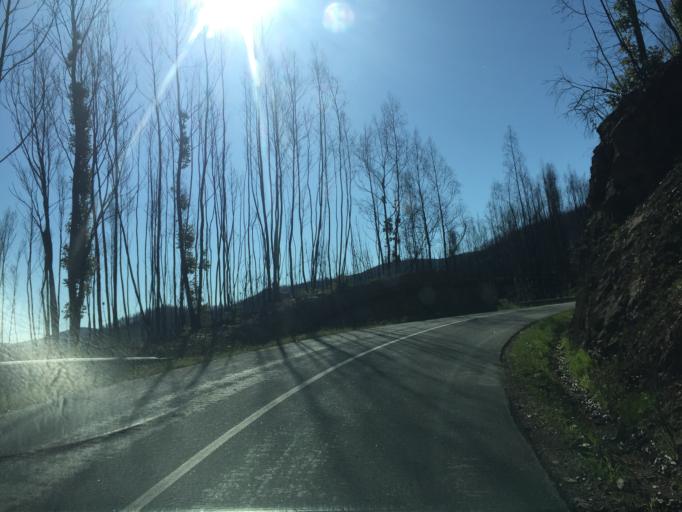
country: PT
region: Coimbra
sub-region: Pampilhosa da Serra
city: Pampilhosa da Serra
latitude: 40.0396
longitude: -7.9395
